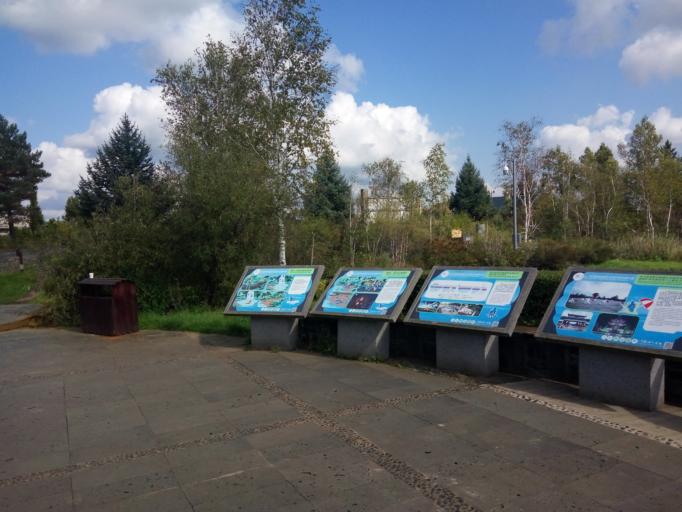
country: CN
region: Heilongjiang Sheng
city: Erjing
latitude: 48.6523
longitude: 126.1476
